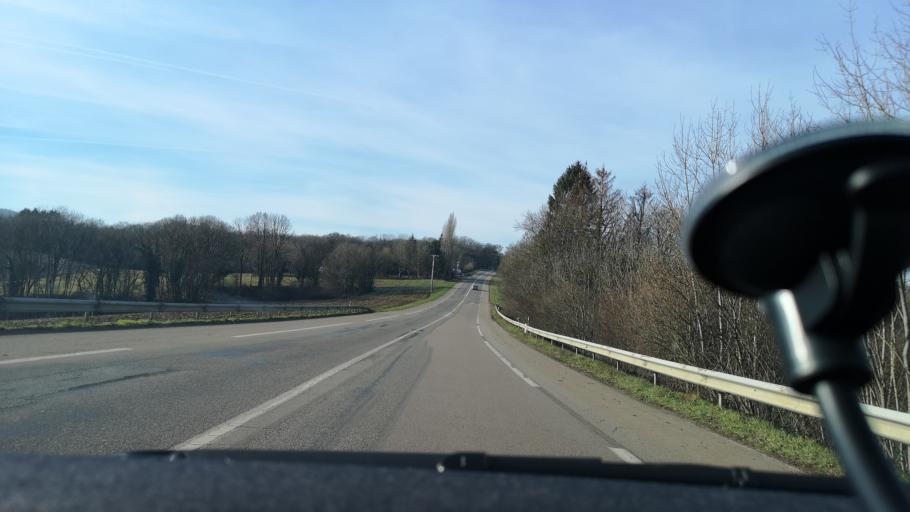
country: FR
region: Franche-Comte
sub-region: Departement du Doubs
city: Baume-les-Dames
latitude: 47.3399
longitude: 6.3031
